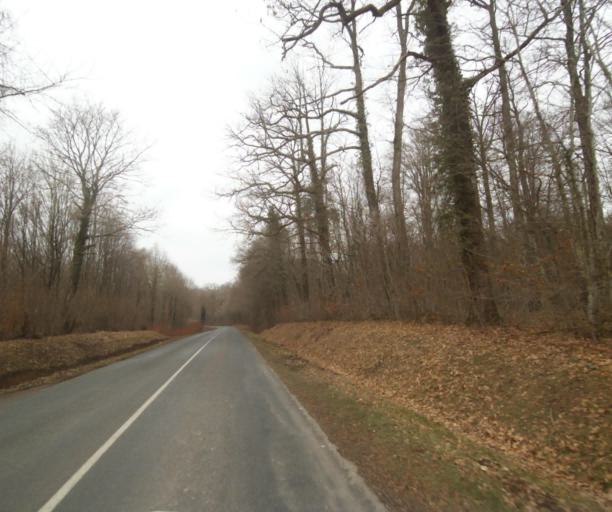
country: FR
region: Champagne-Ardenne
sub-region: Departement de la Haute-Marne
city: Villiers-en-Lieu
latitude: 48.7065
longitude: 4.8918
